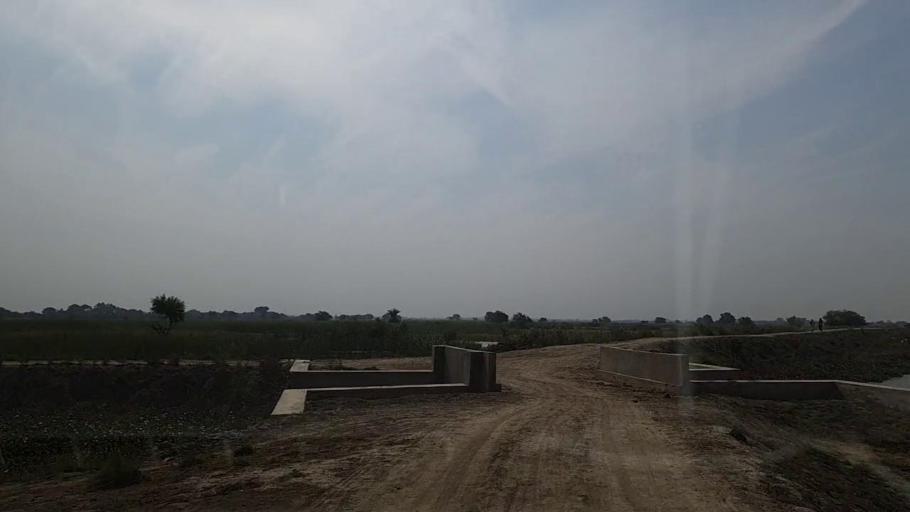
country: PK
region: Sindh
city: Mirpur Batoro
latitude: 24.6619
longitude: 68.2506
